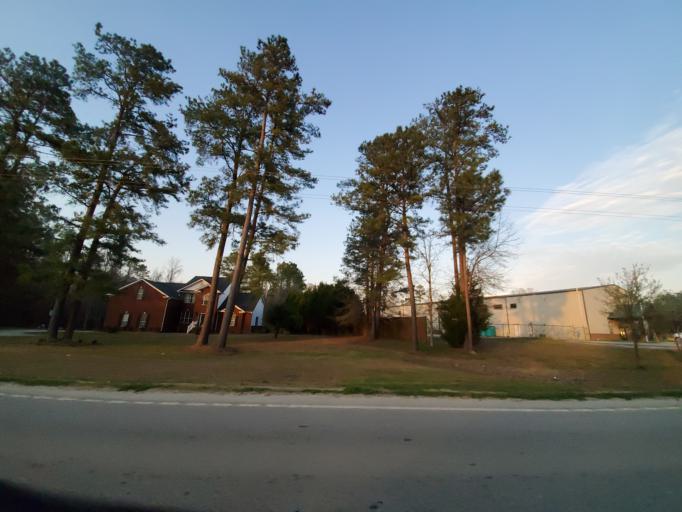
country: US
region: South Carolina
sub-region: Dorchester County
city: Ridgeville
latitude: 33.0081
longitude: -80.3309
